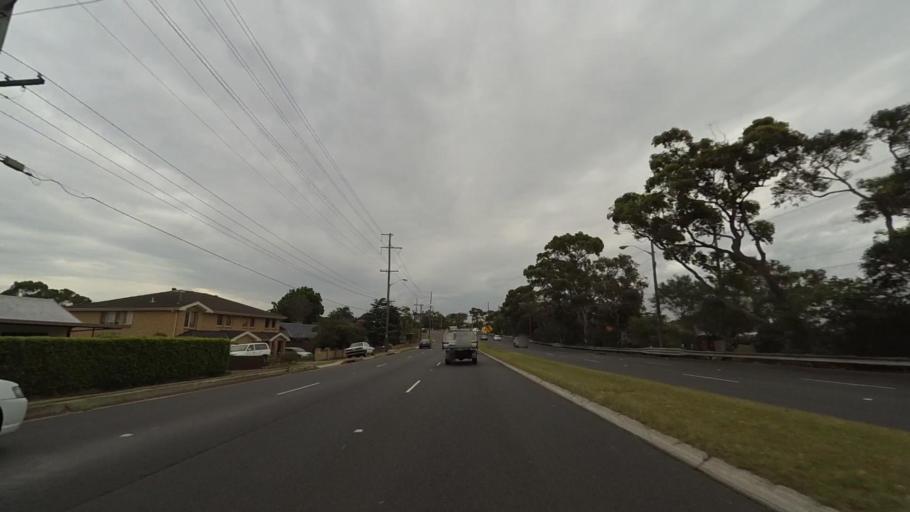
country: AU
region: New South Wales
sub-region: Sutherland Shire
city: Engadine
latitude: -34.0605
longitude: 151.0249
